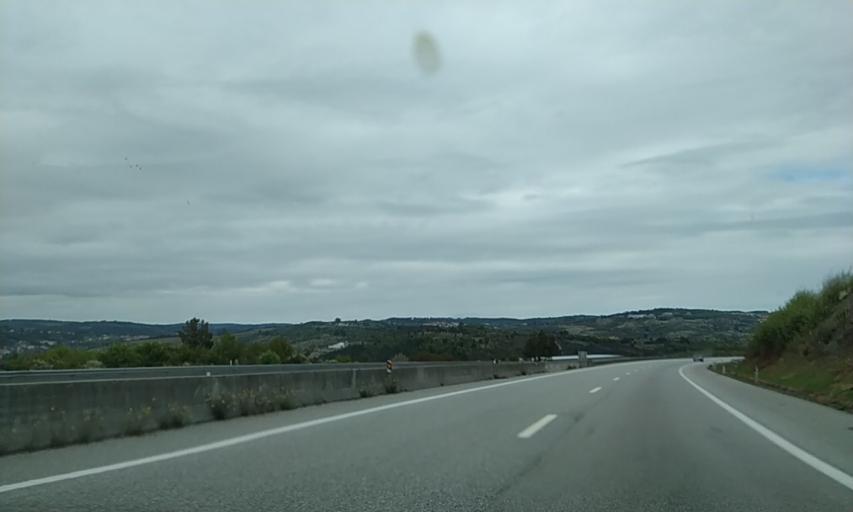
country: PT
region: Viseu
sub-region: Viseu
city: Rio de Loba
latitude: 40.6323
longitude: -7.8375
